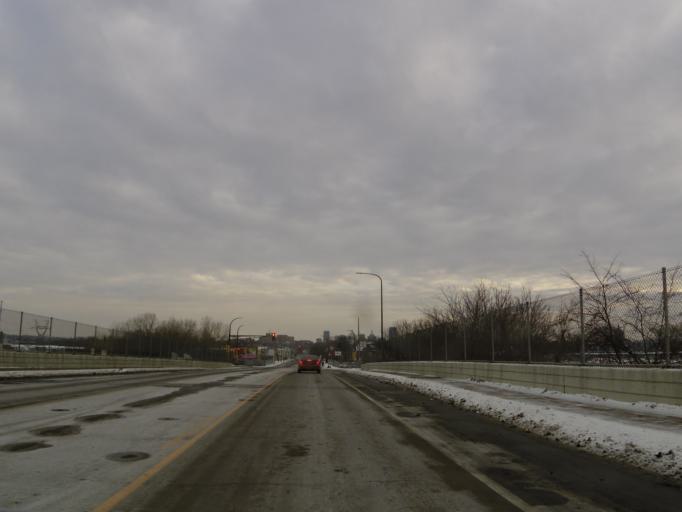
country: US
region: Minnesota
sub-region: Ramsey County
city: Saint Paul
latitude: 44.9652
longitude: -93.1174
